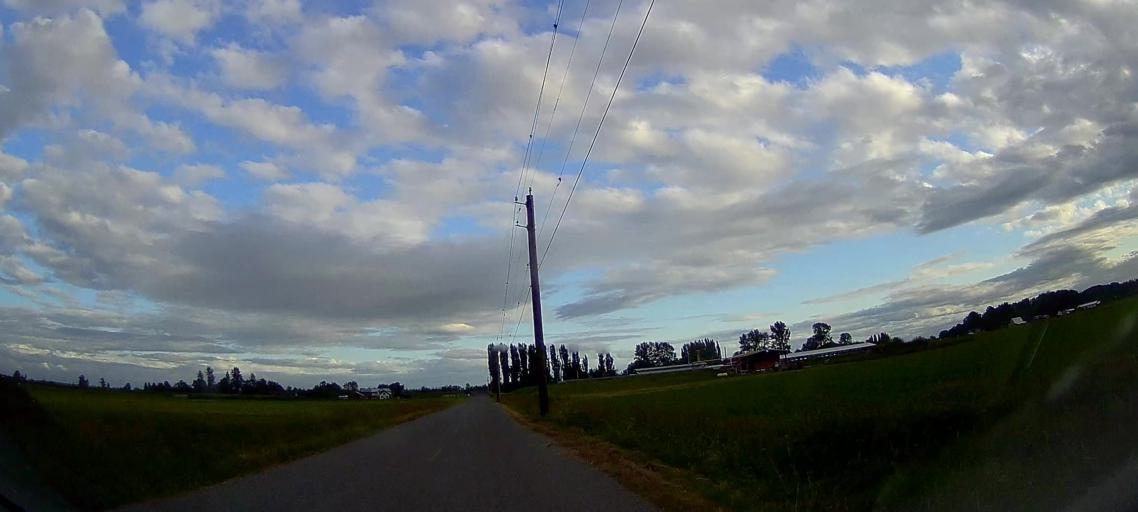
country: US
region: Washington
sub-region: Skagit County
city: Mount Vernon
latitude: 48.3736
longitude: -122.4004
